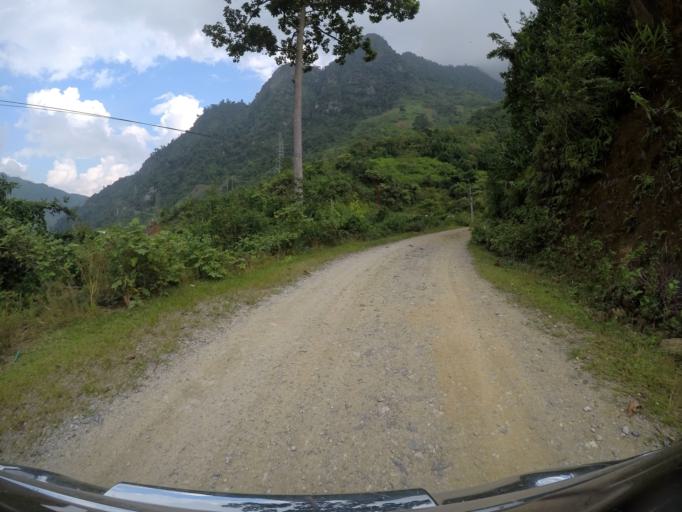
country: VN
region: Yen Bai
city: Son Thinh
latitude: 21.6820
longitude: 104.5604
